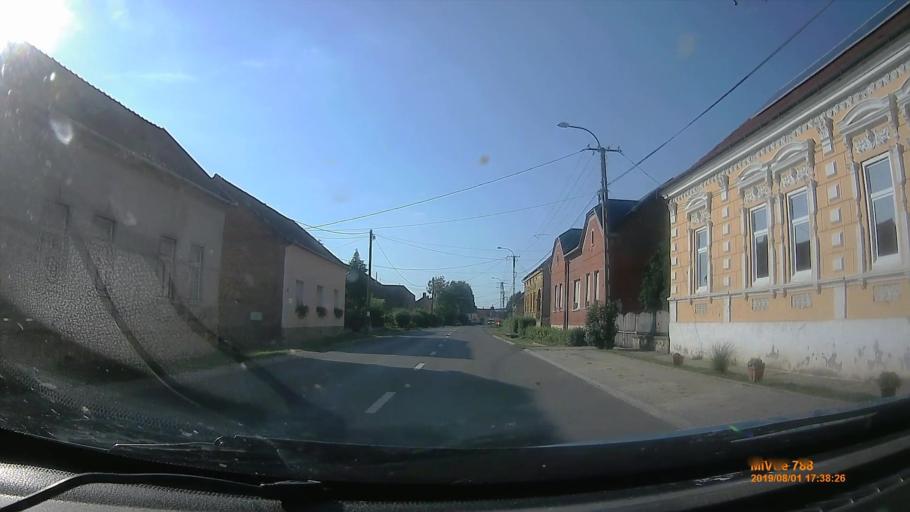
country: HU
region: Baranya
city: Komlo
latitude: 46.1947
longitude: 18.1987
